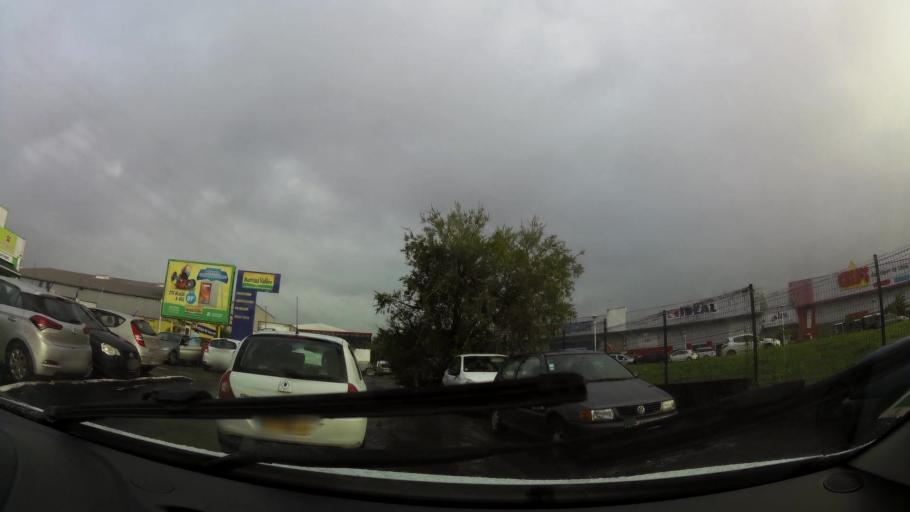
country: RE
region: Reunion
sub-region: Reunion
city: Saint-Andre
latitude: -20.9608
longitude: 55.6599
